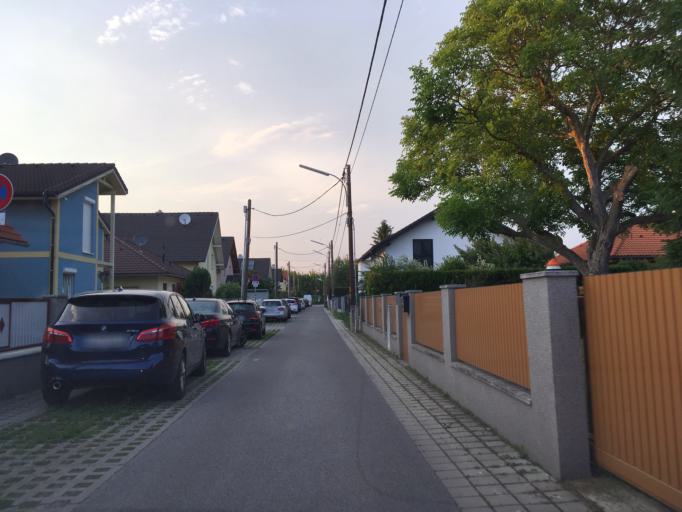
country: AT
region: Lower Austria
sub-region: Politischer Bezirk Wien-Umgebung
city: Gerasdorf bei Wien
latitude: 48.2785
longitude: 16.4612
